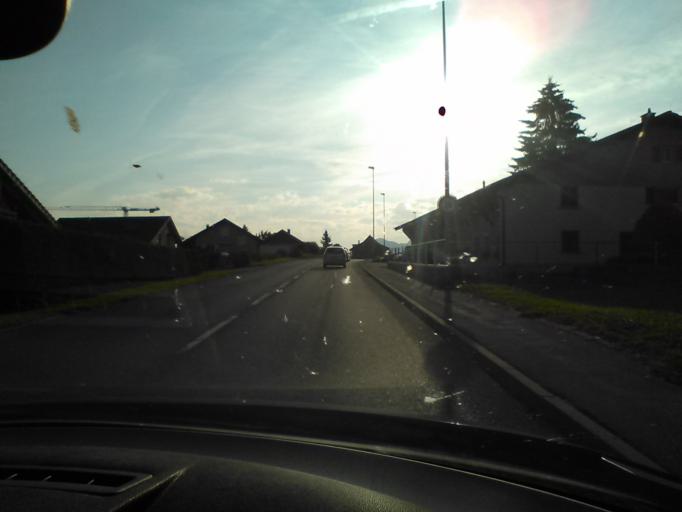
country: CH
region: Fribourg
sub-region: Gruyere District
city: Vuadens
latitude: 46.6183
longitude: 7.0104
